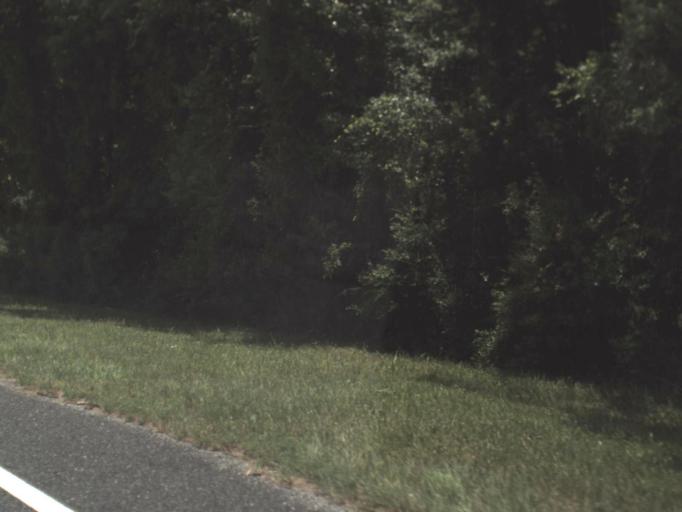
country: US
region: Florida
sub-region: Dixie County
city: Cross City
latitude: 29.6522
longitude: -83.1710
